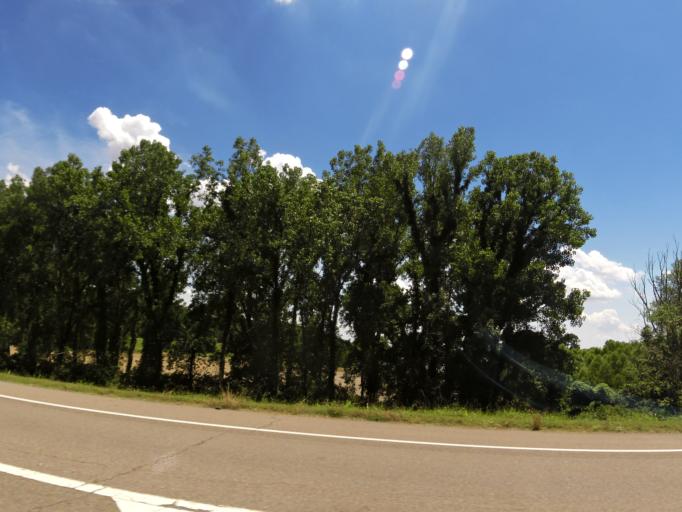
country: US
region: Tennessee
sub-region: Dyer County
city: Dyersburg
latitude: 36.0758
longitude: -89.5003
